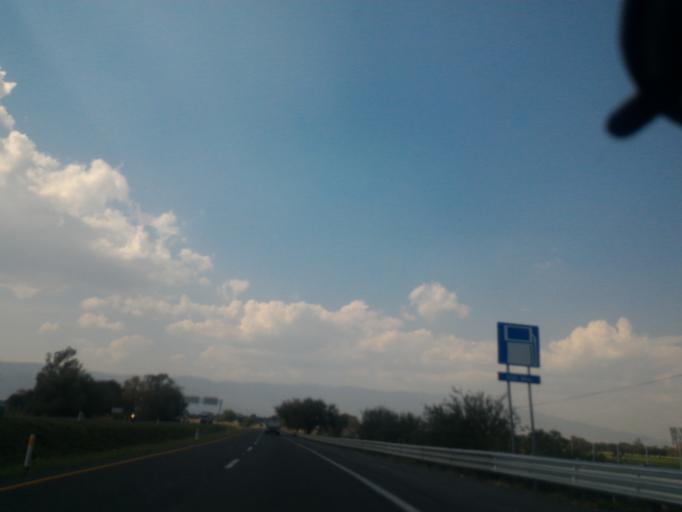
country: MX
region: Jalisco
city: Usmajac
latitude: 19.8898
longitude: -103.5180
